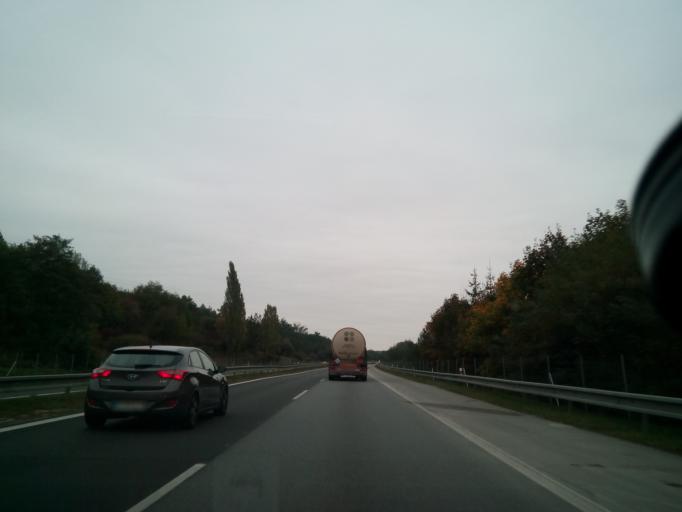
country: SK
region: Kosicky
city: Kosice
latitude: 48.7551
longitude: 21.2796
